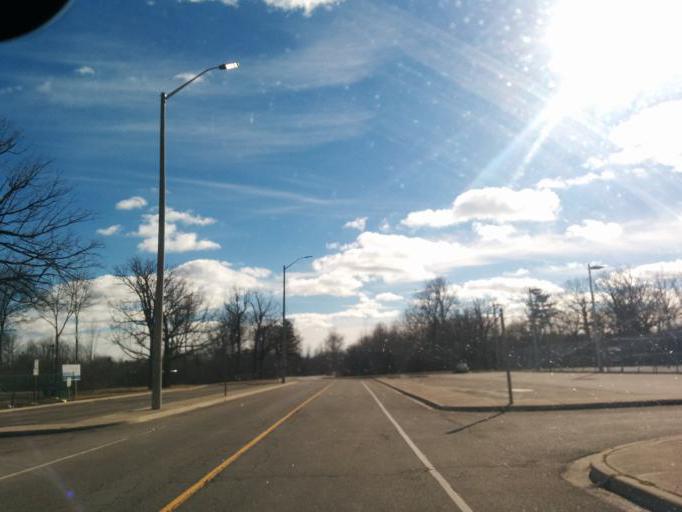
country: CA
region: Ontario
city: Mississauga
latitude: 43.5580
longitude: -79.6315
